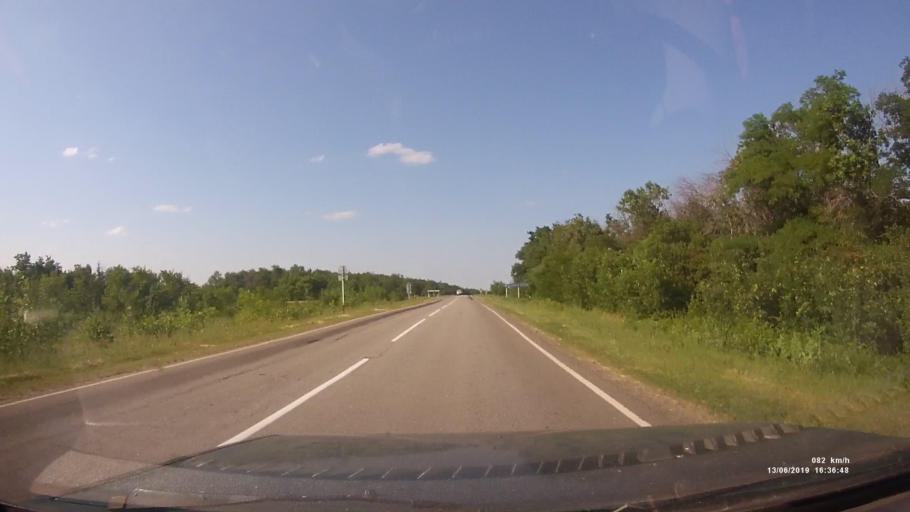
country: RU
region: Rostov
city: Kazanskaya
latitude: 49.8994
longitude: 41.3085
